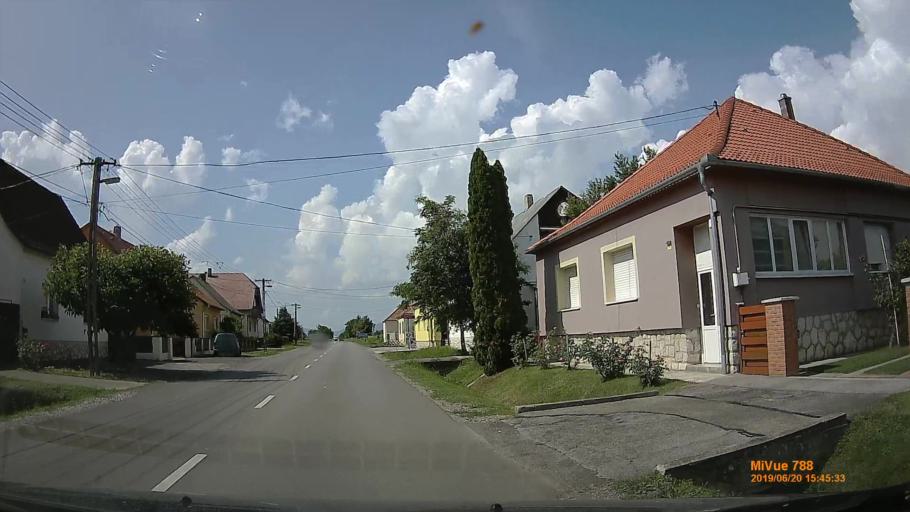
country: HU
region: Baranya
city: Kozarmisleny
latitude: 45.9869
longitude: 18.2484
